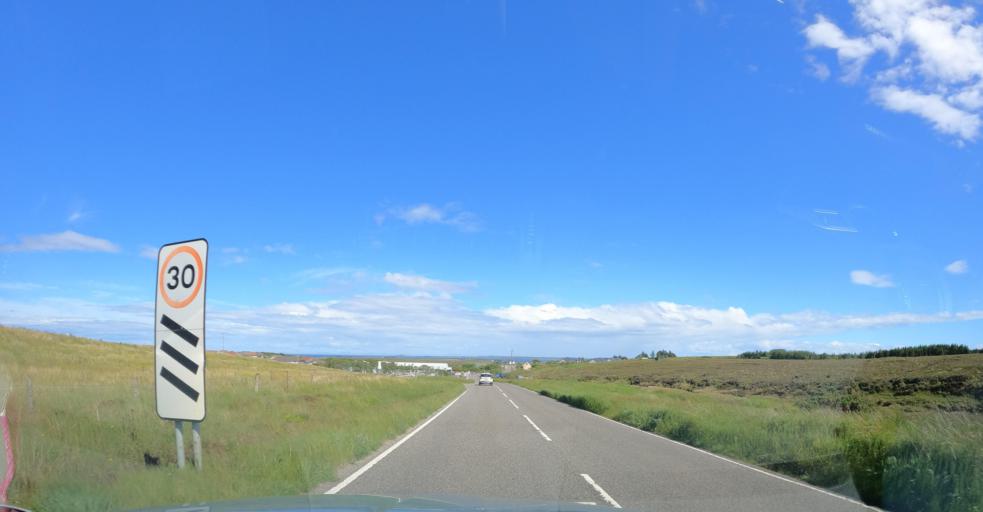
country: GB
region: Scotland
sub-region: Eilean Siar
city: Isle of Lewis
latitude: 58.2482
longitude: -6.4052
